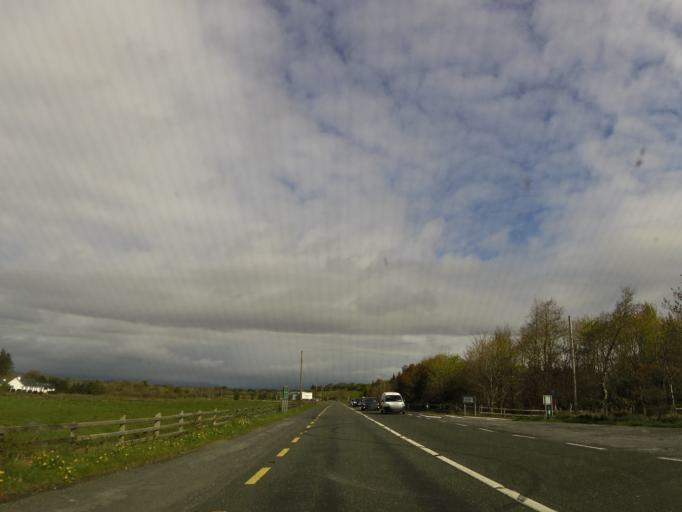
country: IE
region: Connaught
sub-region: Sligo
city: Tobercurry
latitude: 53.9426
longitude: -8.7906
